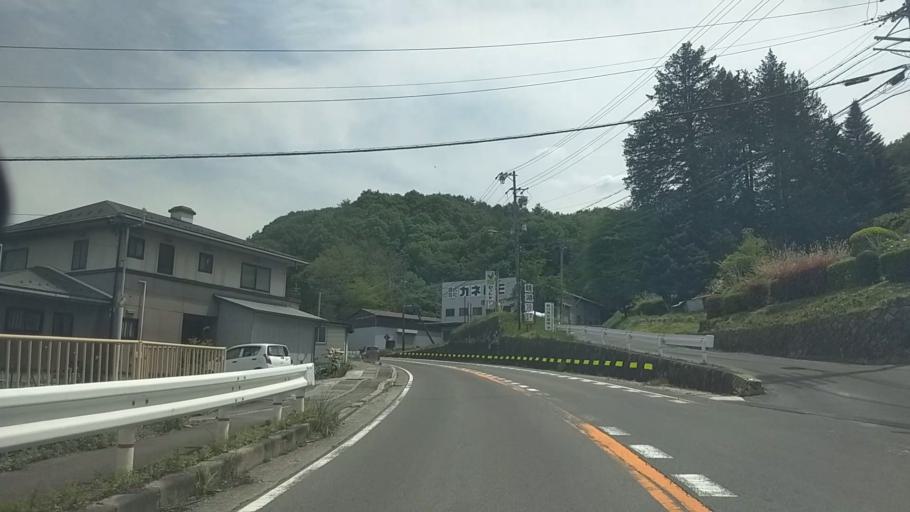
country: JP
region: Nagano
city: Chino
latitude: 35.9775
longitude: 138.1672
